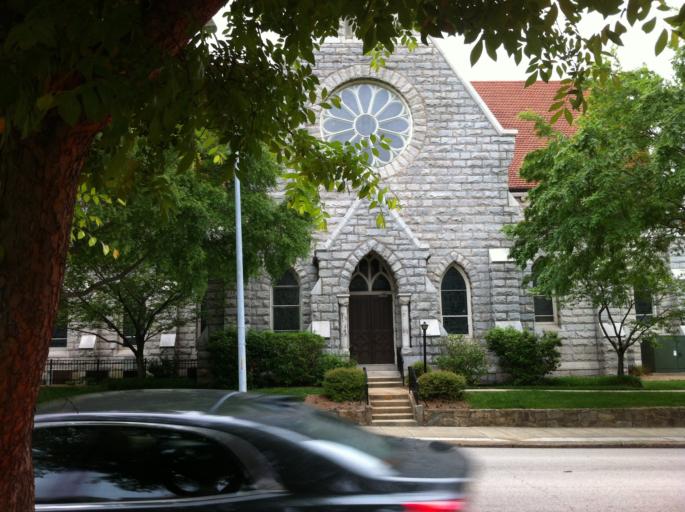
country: US
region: North Carolina
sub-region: Wake County
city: Raleigh
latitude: 35.7802
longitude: -78.6419
